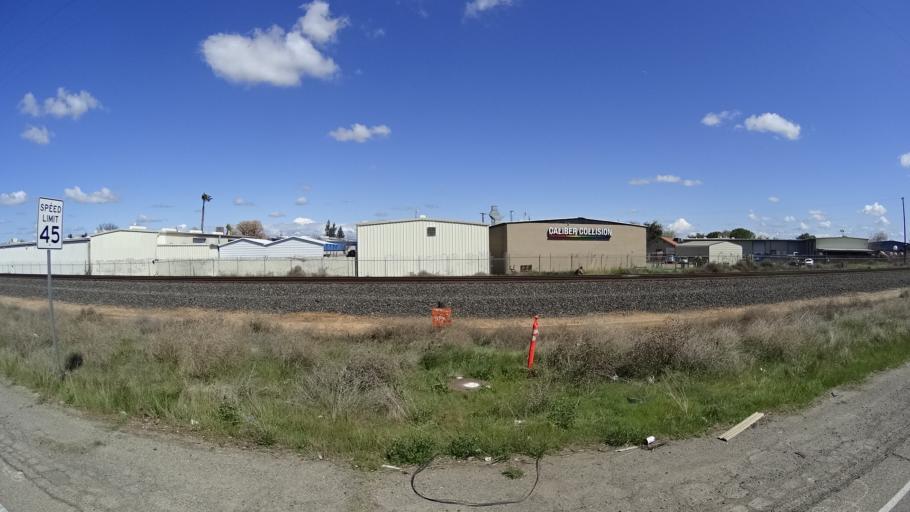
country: US
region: California
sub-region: Fresno County
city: West Park
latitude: 36.8037
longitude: -119.8725
